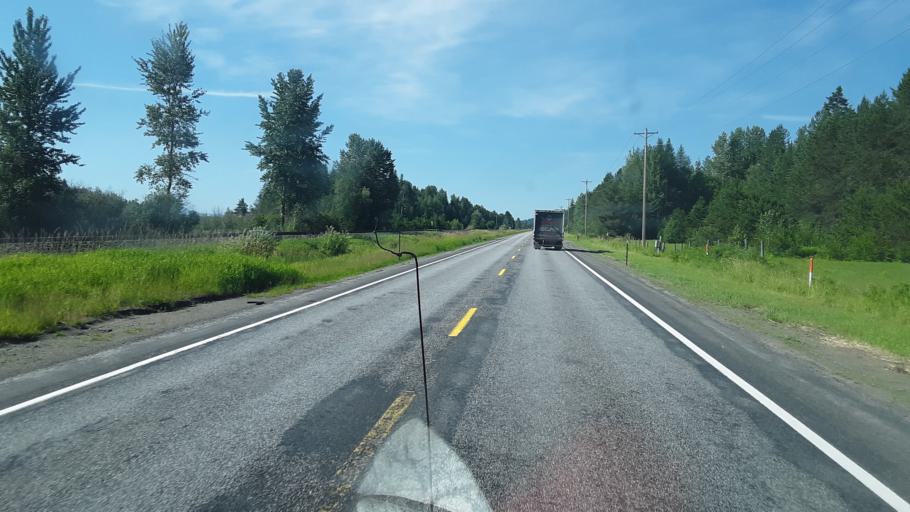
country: US
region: Idaho
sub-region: Bonner County
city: Ponderay
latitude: 48.4726
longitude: -116.4670
